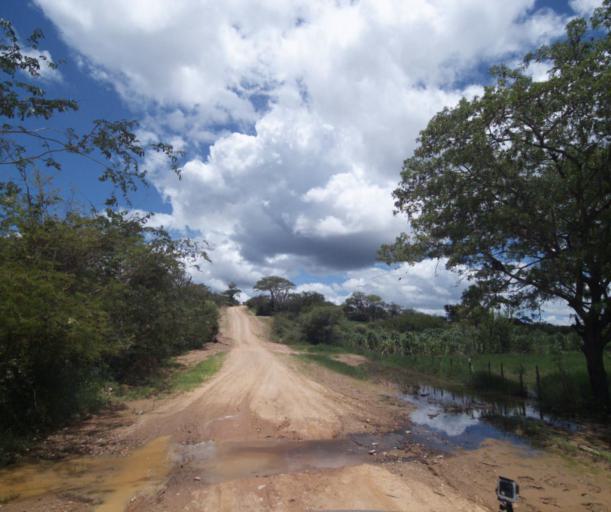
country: BR
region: Bahia
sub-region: Pocoes
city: Pocoes
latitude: -14.3831
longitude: -40.3705
